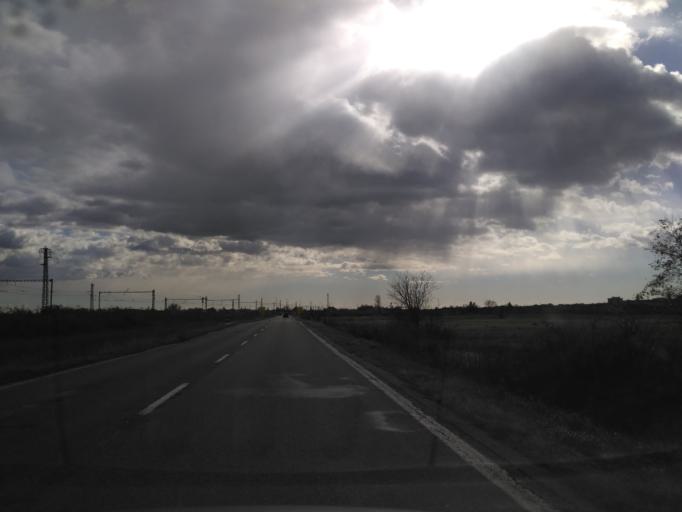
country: HU
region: Borsod-Abauj-Zemplen
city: Satoraljaujhely
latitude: 48.4151
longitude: 21.6647
